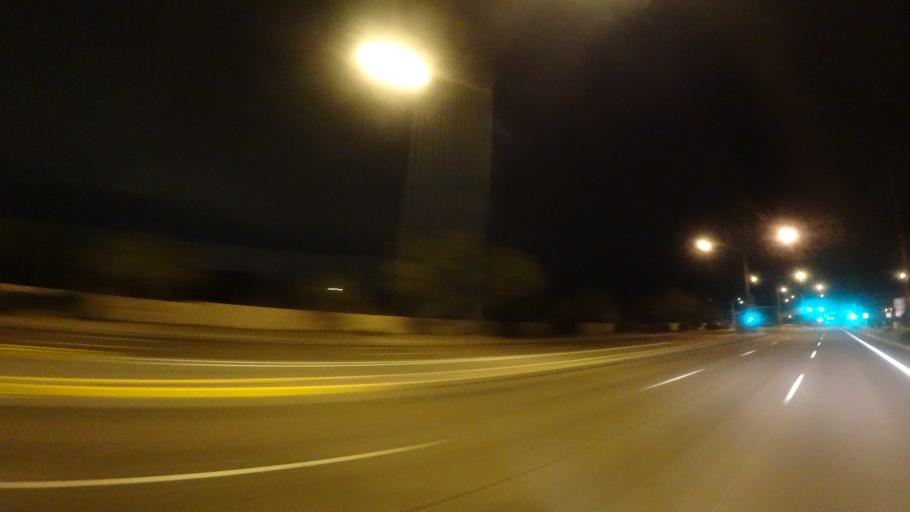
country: US
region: Arizona
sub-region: Pinal County
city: Apache Junction
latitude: 33.4701
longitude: -111.6838
